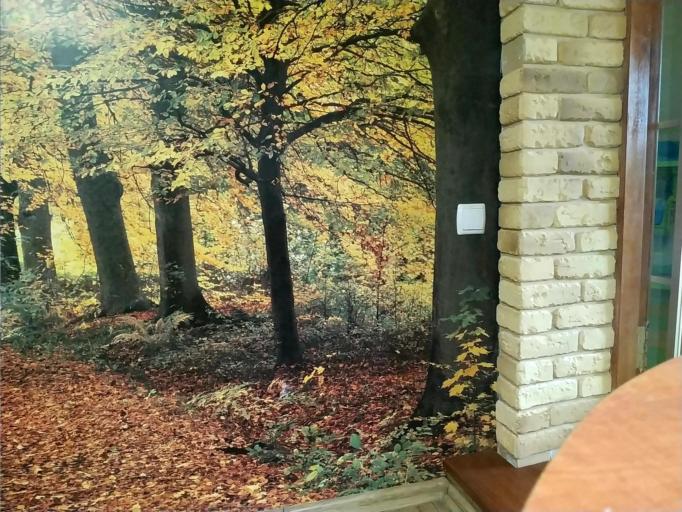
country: RU
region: Smolensk
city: Verkhnedneprovskiy
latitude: 54.9988
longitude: 33.2754
